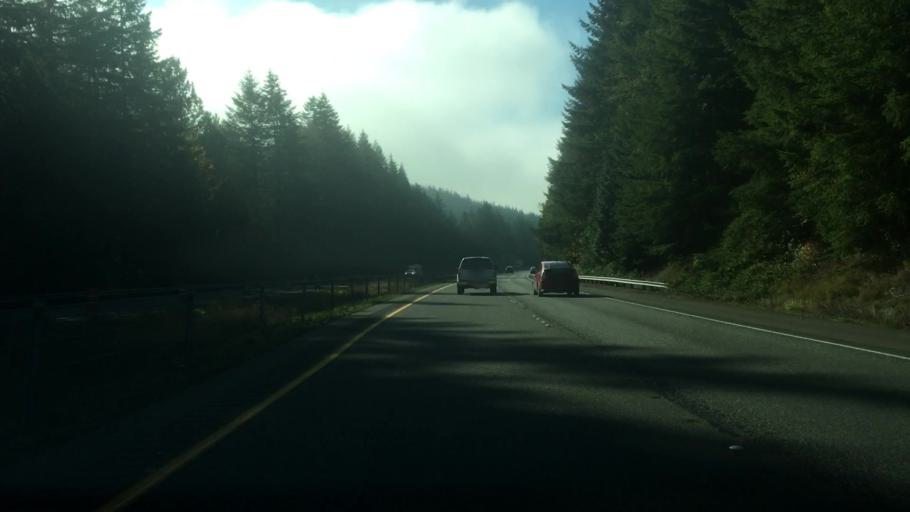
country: US
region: Washington
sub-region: Grays Harbor County
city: McCleary
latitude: 47.0420
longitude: -123.3199
